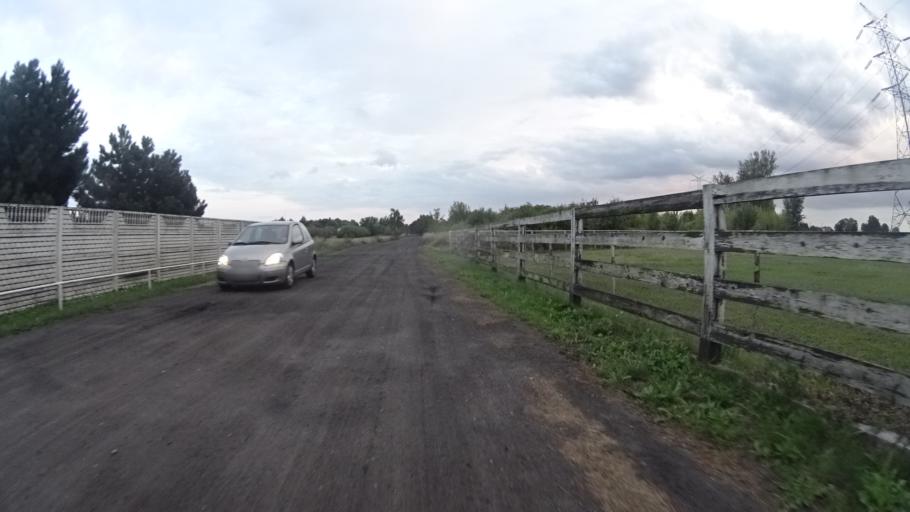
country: PL
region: Masovian Voivodeship
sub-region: Powiat warszawski zachodni
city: Ozarow Mazowiecki
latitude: 52.2353
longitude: 20.7656
